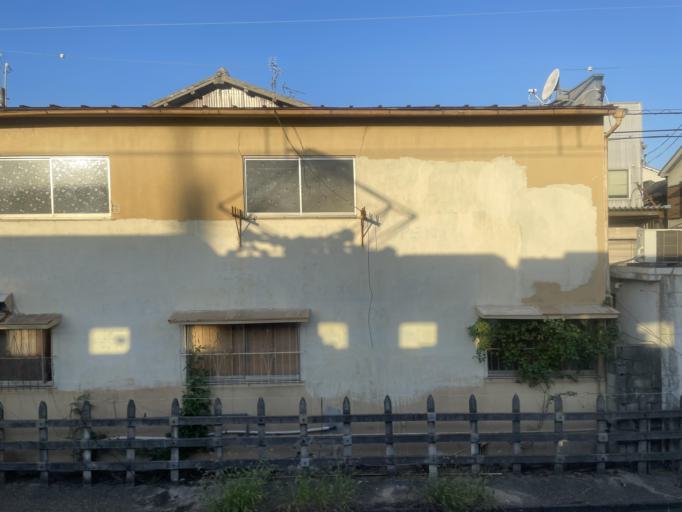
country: JP
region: Osaka
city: Matsubara
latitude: 34.5901
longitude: 135.5340
